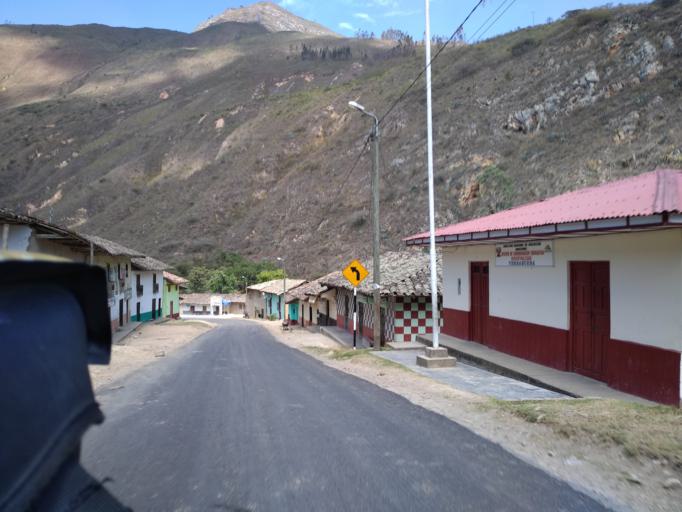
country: PE
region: Amazonas
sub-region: Provincia de Chachapoyas
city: Duraznopampa
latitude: -6.5613
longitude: -77.8293
